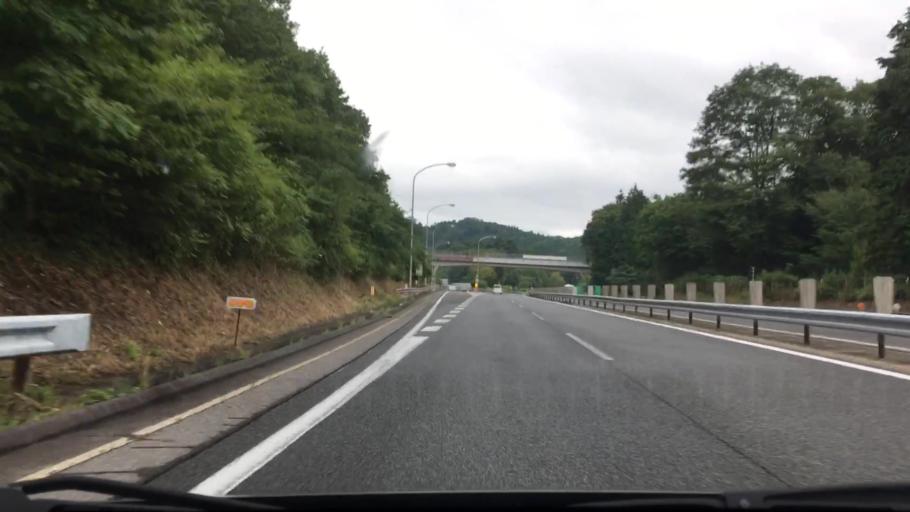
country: JP
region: Hiroshima
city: Miyoshi
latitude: 34.6978
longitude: 132.6028
